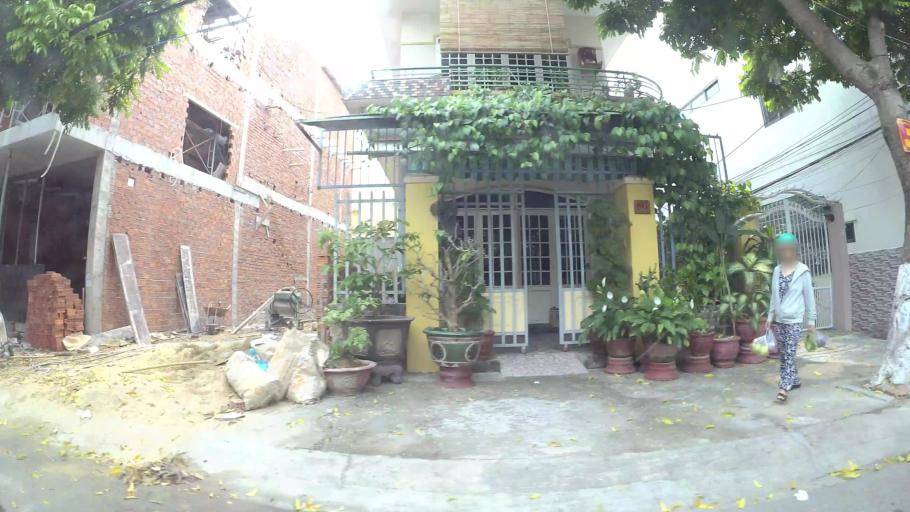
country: VN
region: Da Nang
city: Da Nang
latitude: 16.0822
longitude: 108.2149
